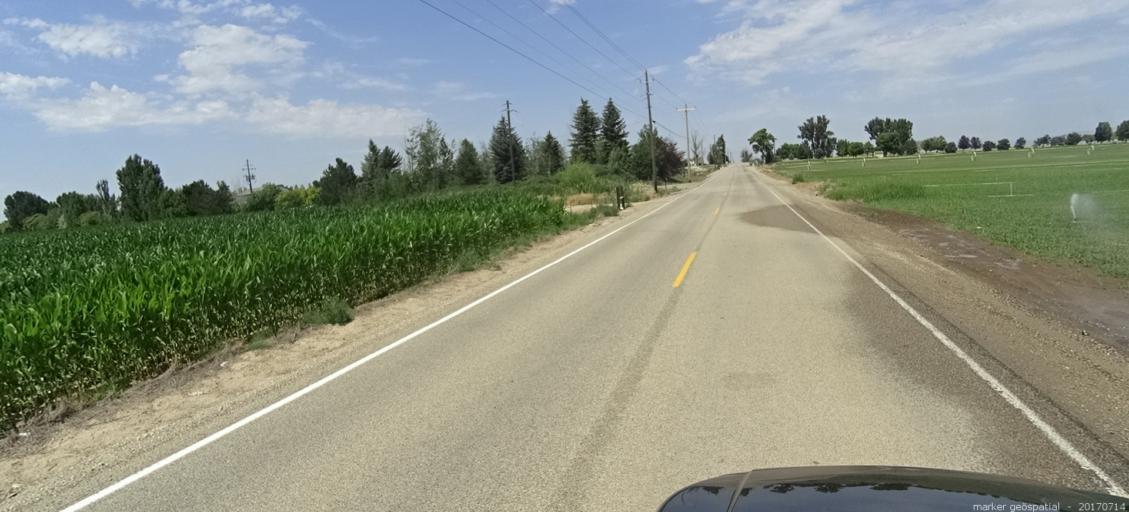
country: US
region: Idaho
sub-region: Ada County
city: Kuna
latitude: 43.5368
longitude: -116.3543
